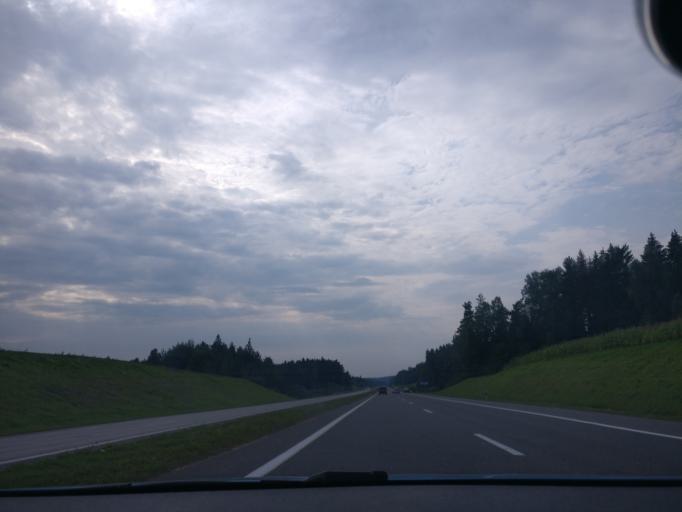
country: BY
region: Minsk
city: Lahoysk
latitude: 54.1408
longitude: 27.8091
